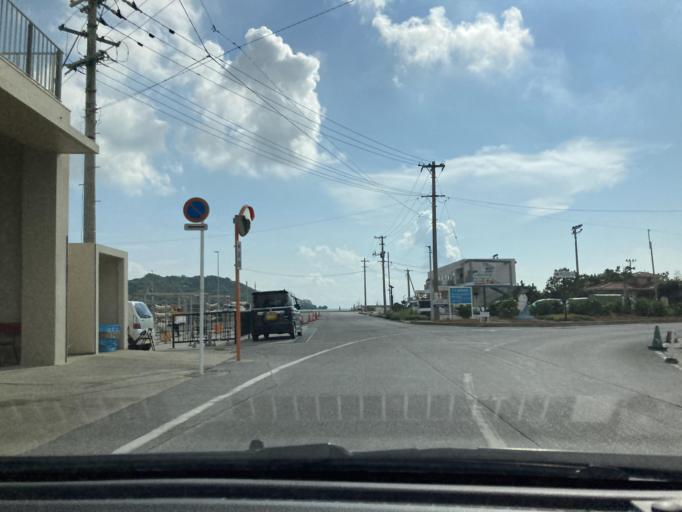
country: JP
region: Okinawa
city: Itoman
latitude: 26.1317
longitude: 127.7737
